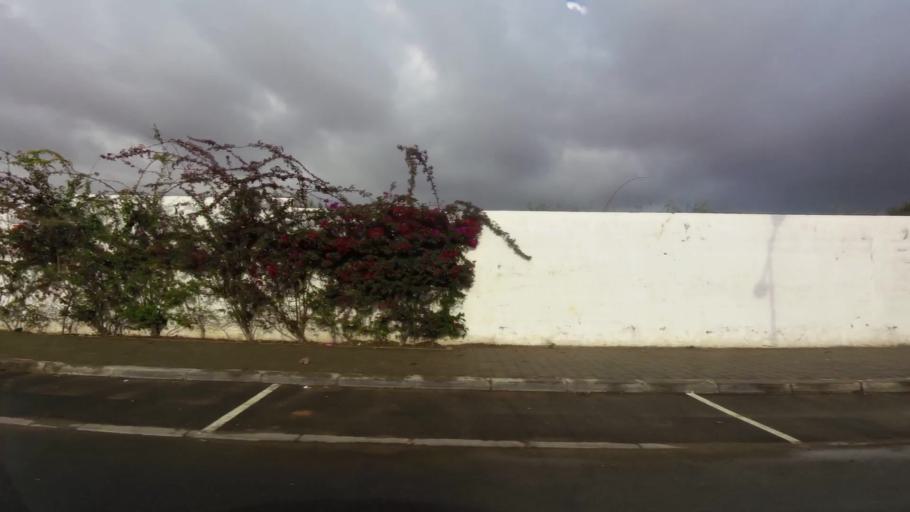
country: MA
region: Grand Casablanca
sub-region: Casablanca
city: Casablanca
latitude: 33.5526
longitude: -7.6514
